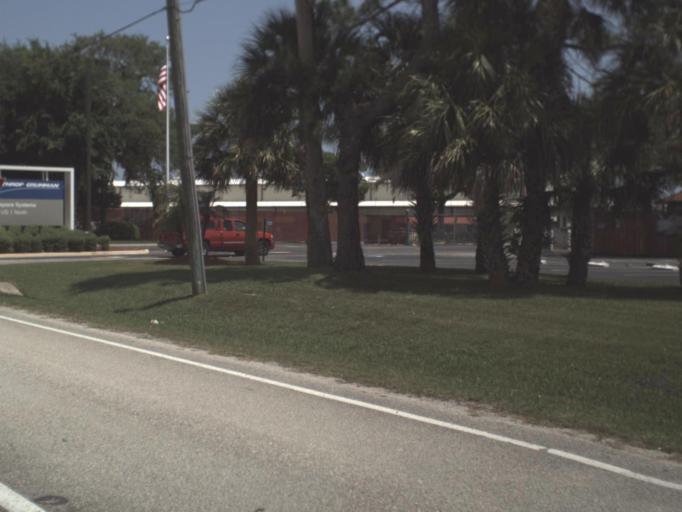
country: US
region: Florida
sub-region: Saint Johns County
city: Villano Beach
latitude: 29.9613
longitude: -81.3477
